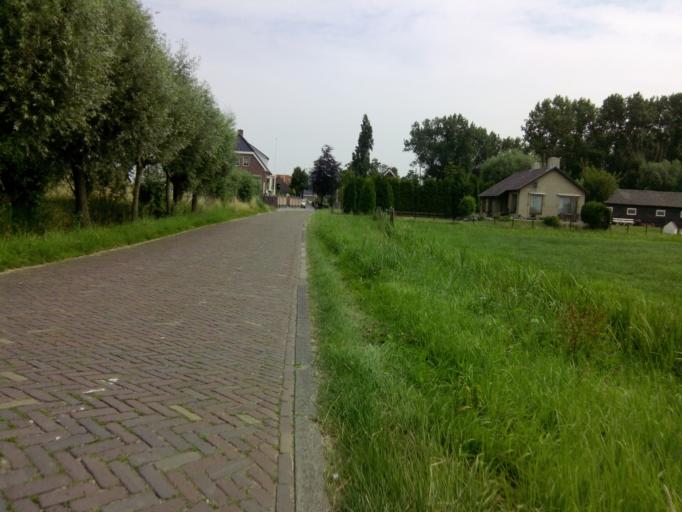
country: NL
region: Utrecht
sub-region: Gemeente Bunschoten
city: Spakenburg
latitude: 52.2637
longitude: 5.3385
